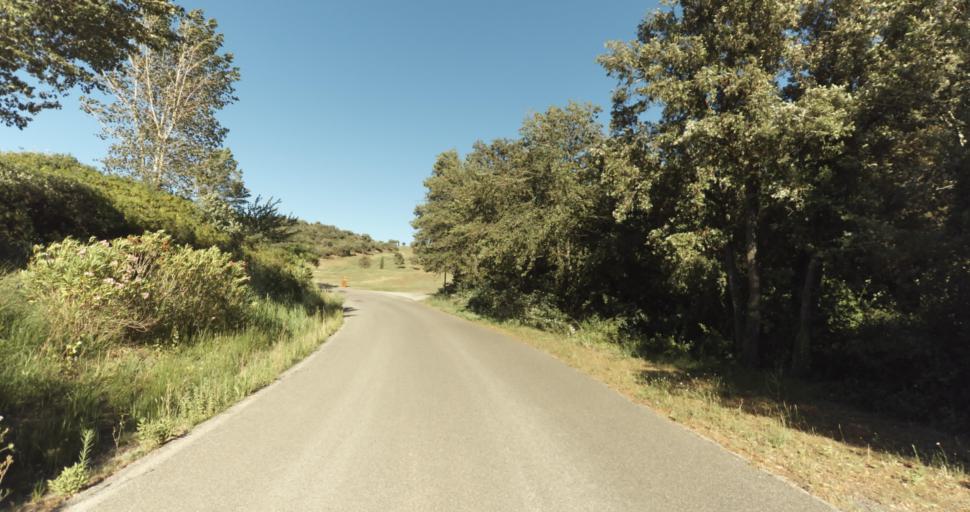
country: FR
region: Provence-Alpes-Cote d'Azur
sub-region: Departement du Var
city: Gassin
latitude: 43.2517
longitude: 6.6054
